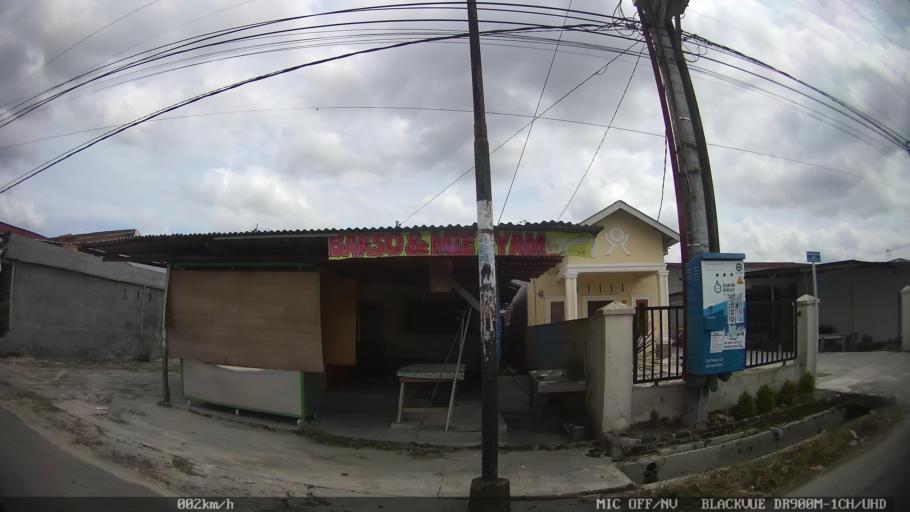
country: ID
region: North Sumatra
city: Percut
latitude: 3.5700
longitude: 98.8645
